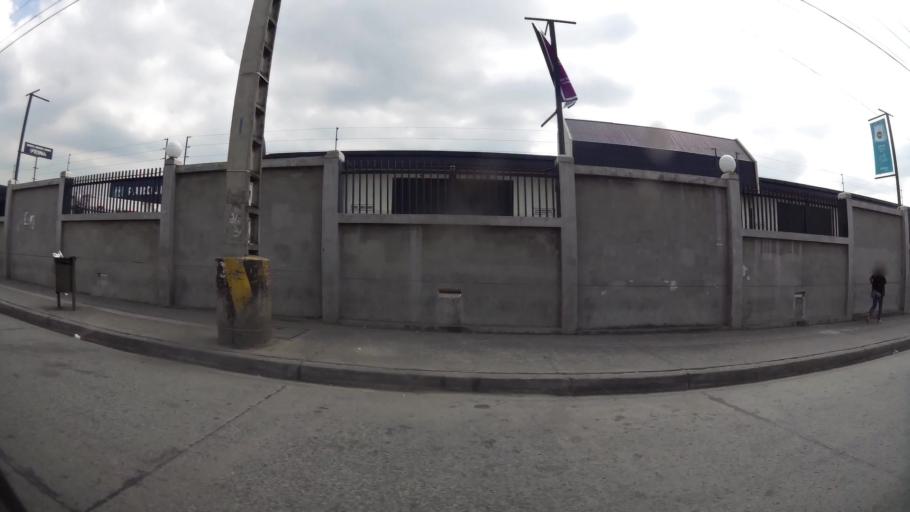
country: EC
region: Guayas
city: Santa Lucia
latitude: -2.0976
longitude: -79.9362
